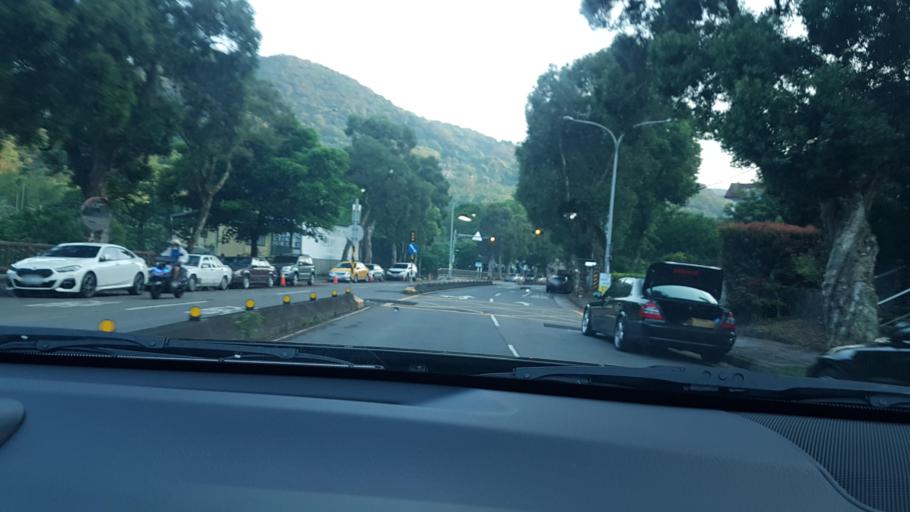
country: TW
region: Taipei
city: Taipei
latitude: 25.1060
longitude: 121.5574
